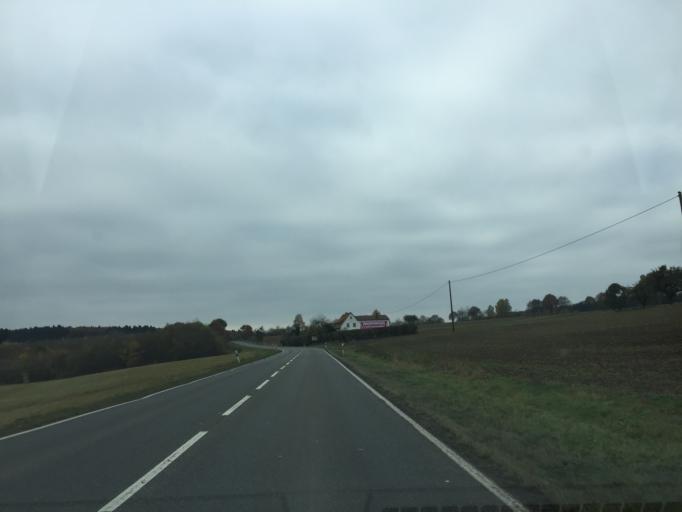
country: DE
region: Rheinland-Pfalz
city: Grossholbach
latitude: 50.4429
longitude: 7.8874
